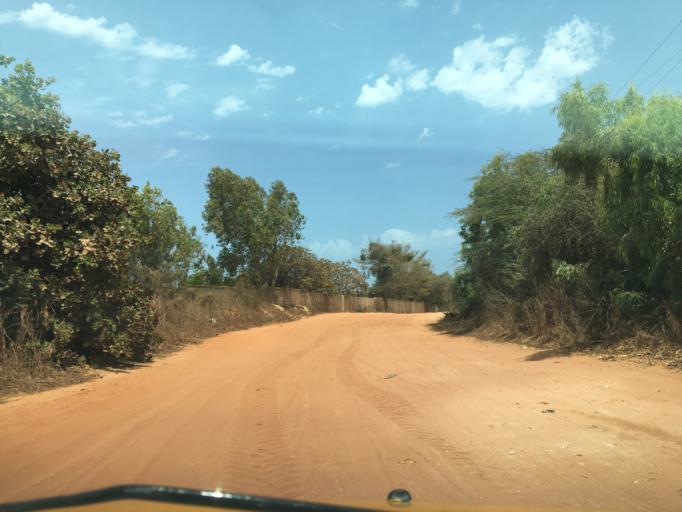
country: SN
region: Thies
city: Thies
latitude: 14.8176
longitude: -17.1979
